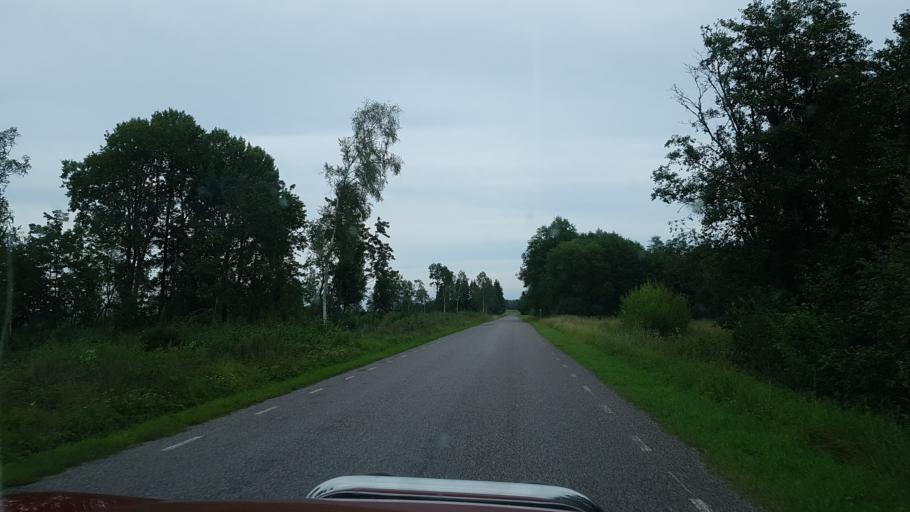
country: EE
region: Laeaene
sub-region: Lihula vald
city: Lihula
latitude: 58.8795
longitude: 23.8231
